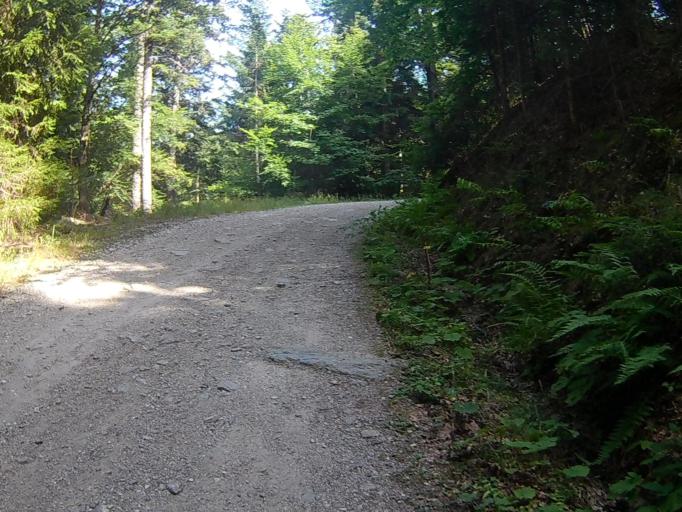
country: SI
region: Ruse
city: Ruse
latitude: 46.5141
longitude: 15.5443
